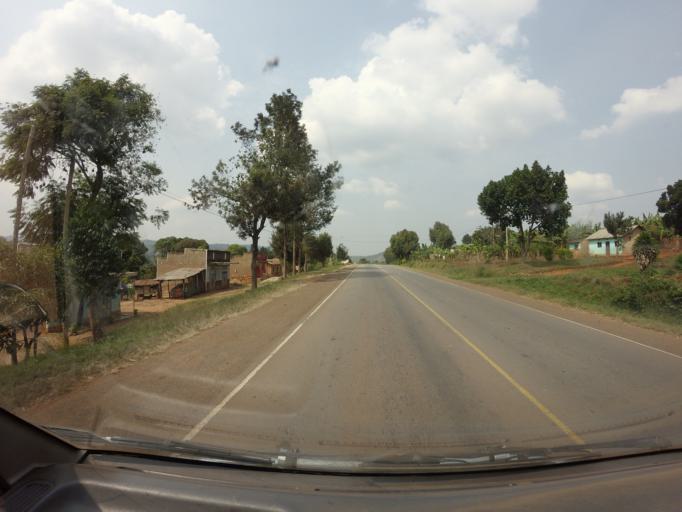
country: UG
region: Central Region
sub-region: Lwengo District
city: Lwengo
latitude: -0.3807
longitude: 31.2915
